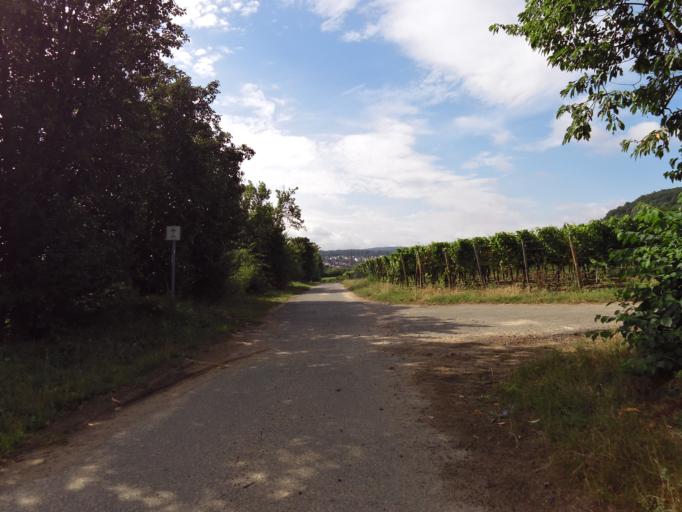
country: DE
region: Rheinland-Pfalz
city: Bad Duerkheim
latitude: 49.4716
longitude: 8.1663
